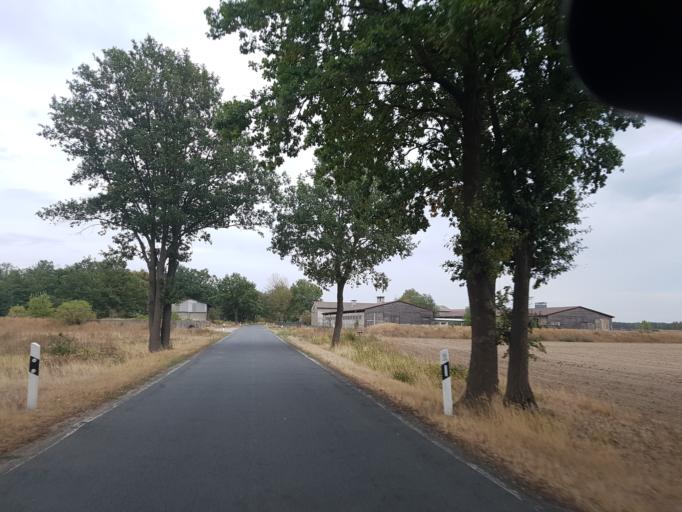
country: DE
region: Saxony-Anhalt
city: Annaburg
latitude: 51.7684
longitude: 13.0719
